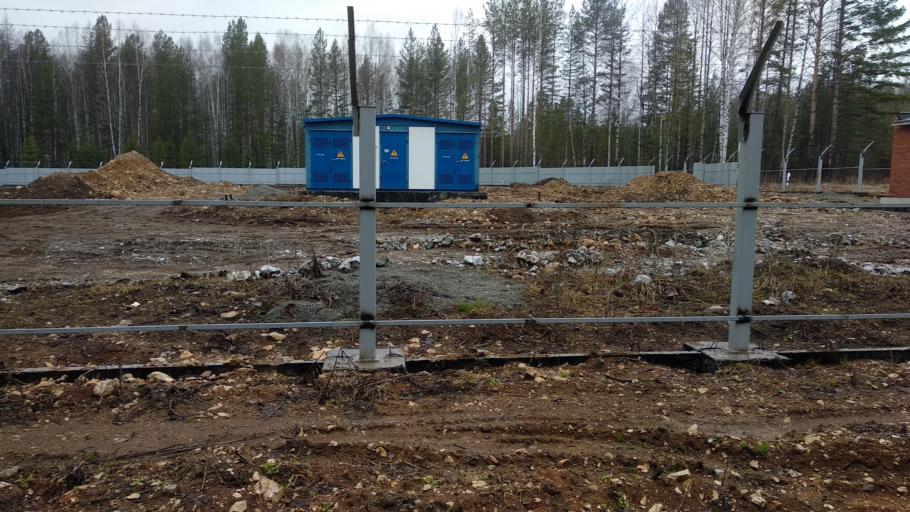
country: RU
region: Sverdlovsk
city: Krasnotur'insk
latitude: 59.6515
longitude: 60.1575
